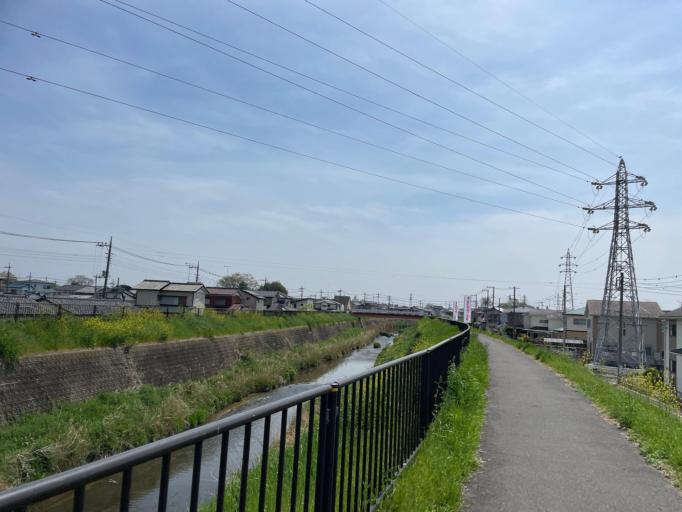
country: JP
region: Saitama
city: Fukayacho
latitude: 36.2037
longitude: 139.2877
